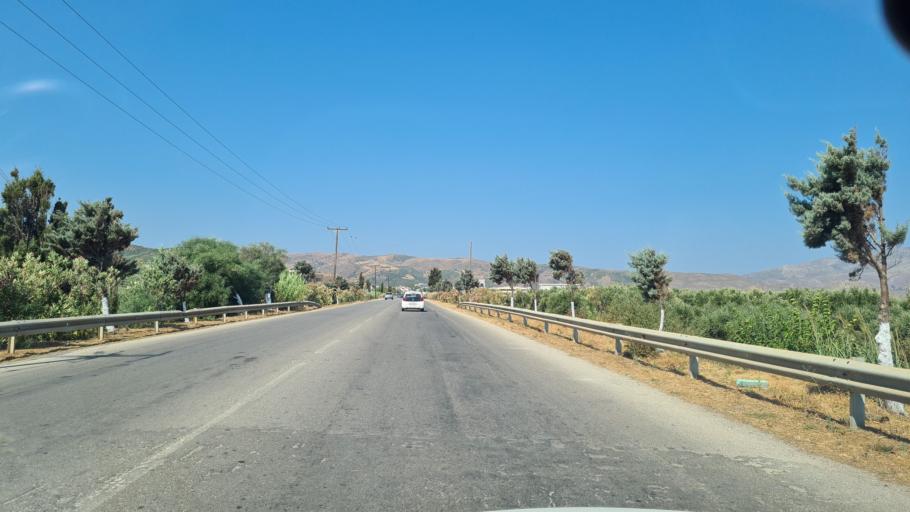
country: GR
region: Crete
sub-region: Nomos Chanias
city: Kissamos
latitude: 35.4948
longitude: 23.6785
